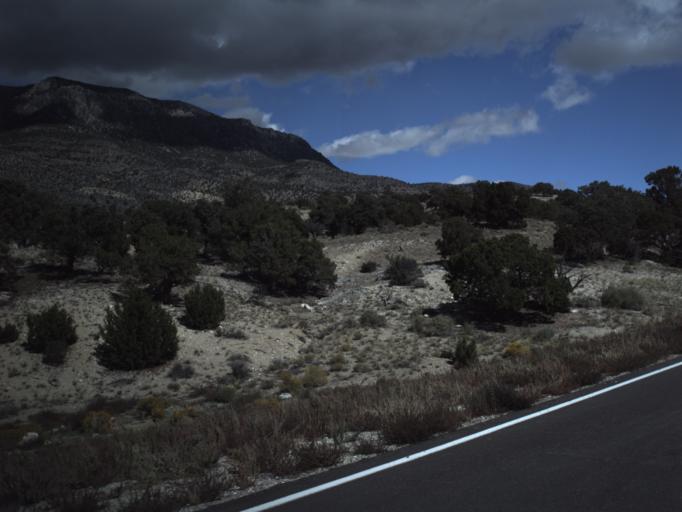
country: US
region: Utah
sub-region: Beaver County
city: Milford
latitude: 38.5151
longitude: -113.5611
